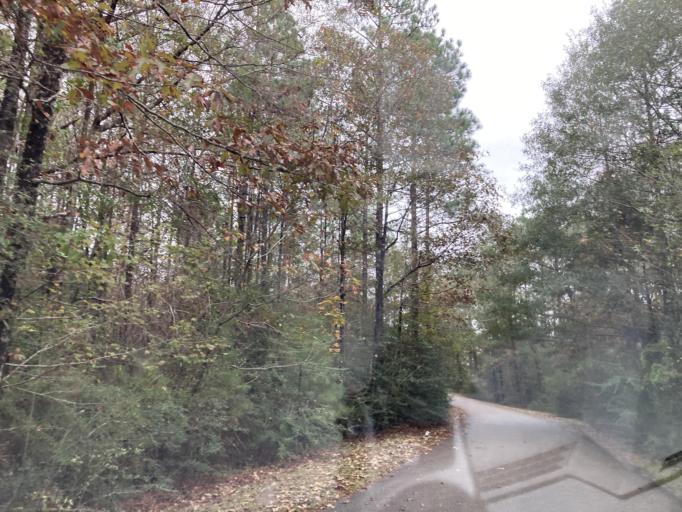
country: US
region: Mississippi
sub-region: Lamar County
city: West Hattiesburg
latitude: 31.2866
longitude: -89.4803
